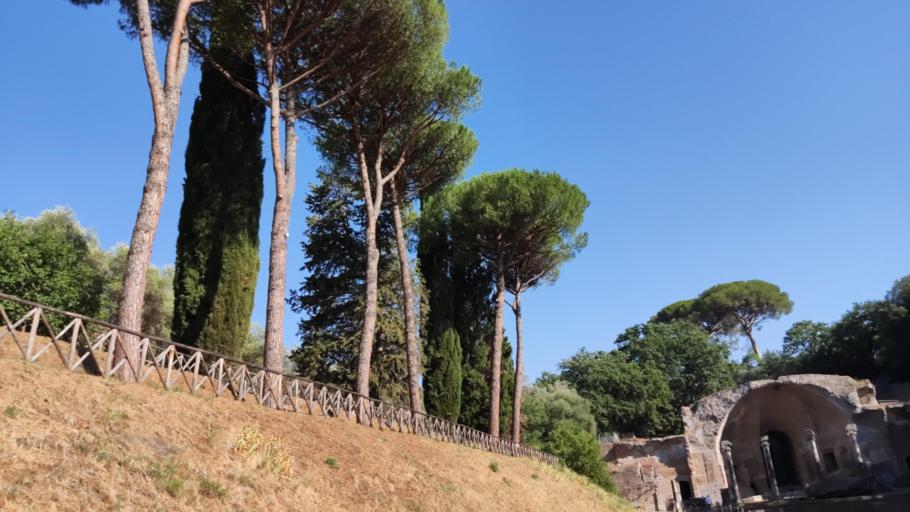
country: IT
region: Latium
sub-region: Citta metropolitana di Roma Capitale
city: Villa Adriana
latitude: 41.9387
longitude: 12.7760
